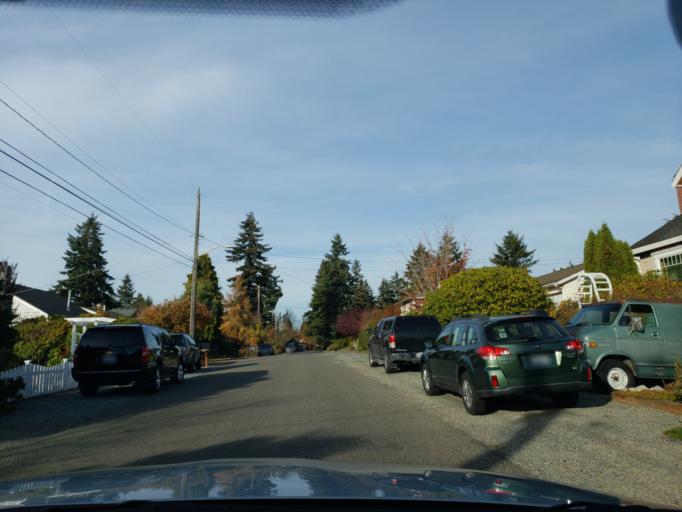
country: US
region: Washington
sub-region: King County
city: Shoreline
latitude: 47.7060
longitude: -122.3581
